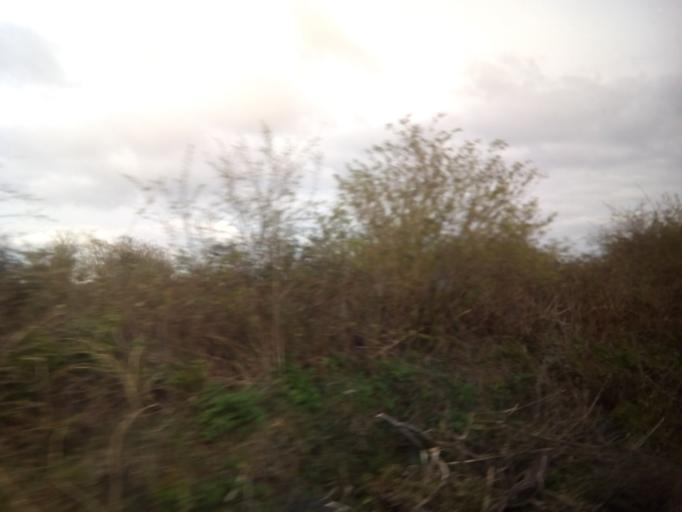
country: IE
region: Leinster
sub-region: Kildare
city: Kilcock
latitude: 53.4105
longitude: -6.6872
